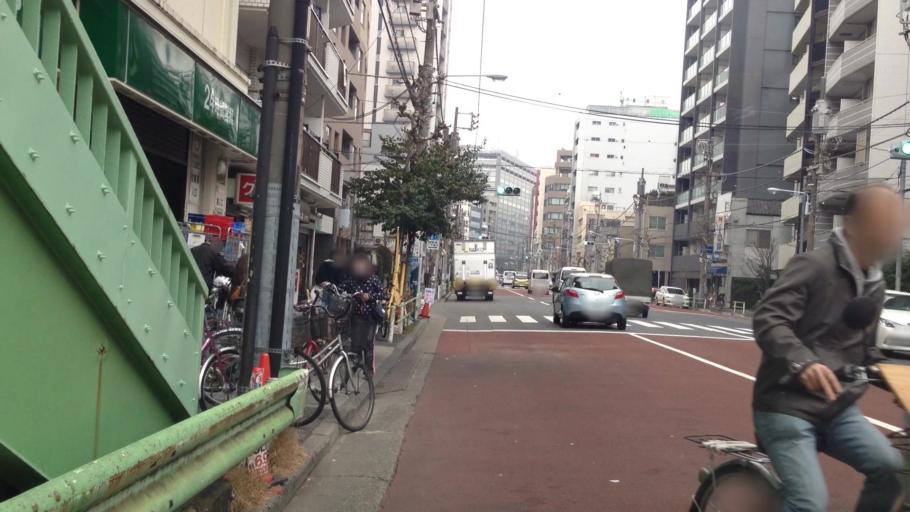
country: JP
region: Tokyo
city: Tokyo
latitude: 35.7137
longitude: 139.7829
